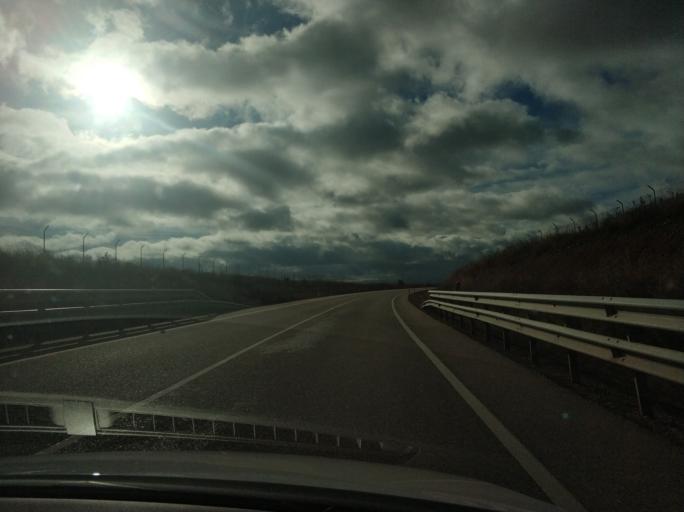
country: ES
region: Castille and Leon
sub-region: Provincia de Segovia
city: Ayllon
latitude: 41.4214
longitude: -3.3962
